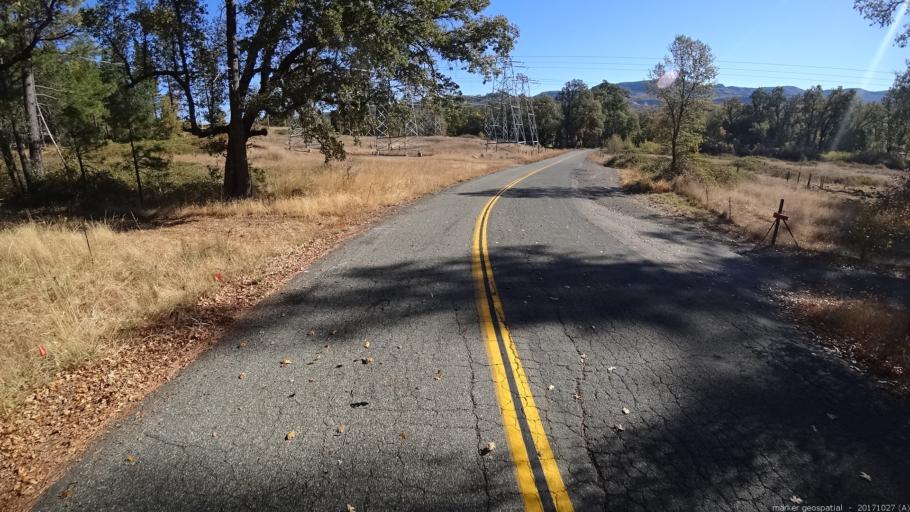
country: US
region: California
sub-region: Shasta County
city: Burney
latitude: 40.8245
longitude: -121.9344
